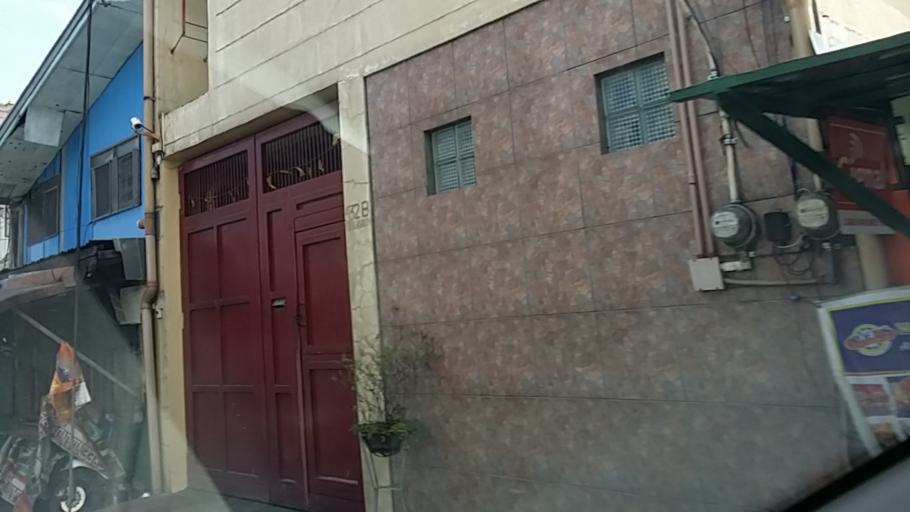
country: PH
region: Metro Manila
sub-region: Mandaluyong
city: Mandaluyong City
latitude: 14.5738
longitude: 121.0341
